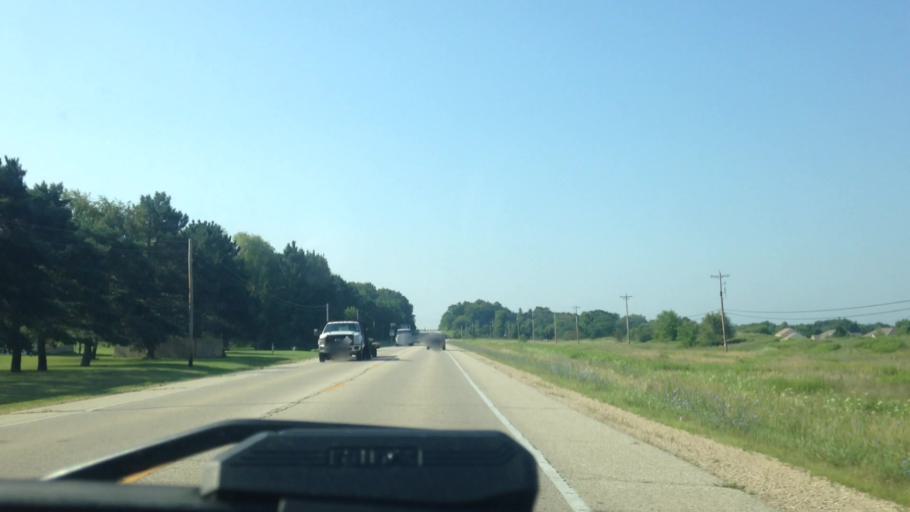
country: US
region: Wisconsin
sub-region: Waukesha County
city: Merton
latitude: 43.2058
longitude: -88.2616
